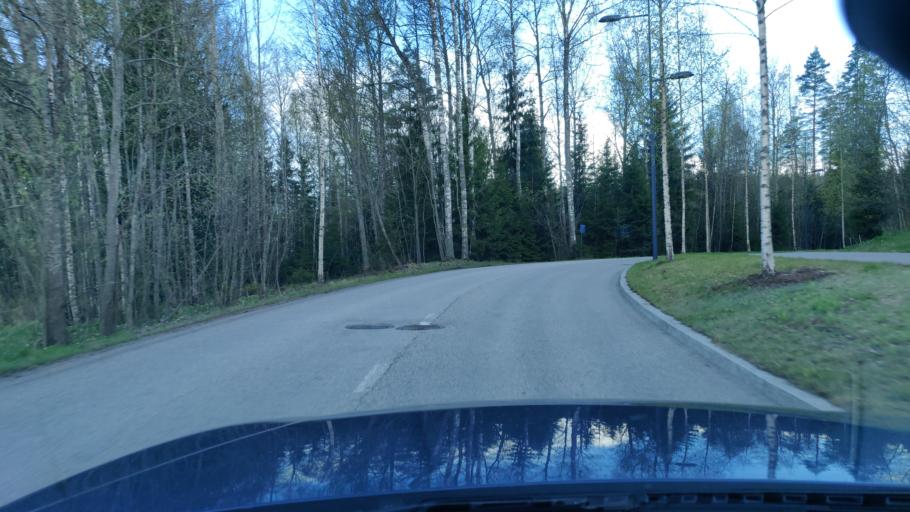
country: FI
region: Uusimaa
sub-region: Helsinki
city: Jaervenpaeae
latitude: 60.4841
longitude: 25.0571
